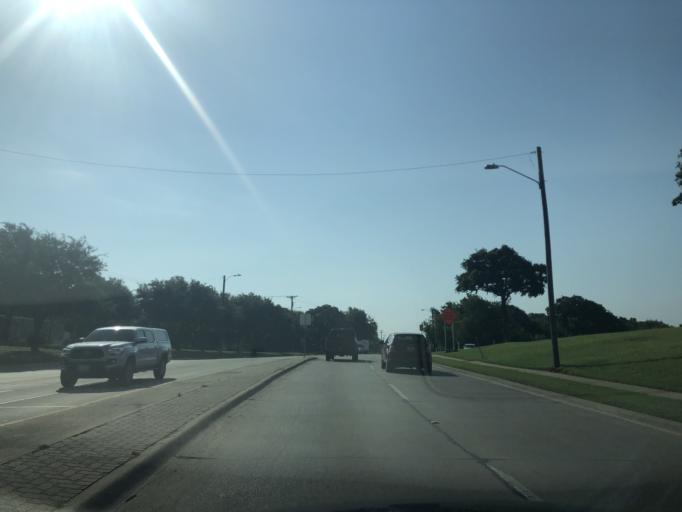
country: US
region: Texas
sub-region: Dallas County
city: Irving
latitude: 32.8049
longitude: -96.9937
